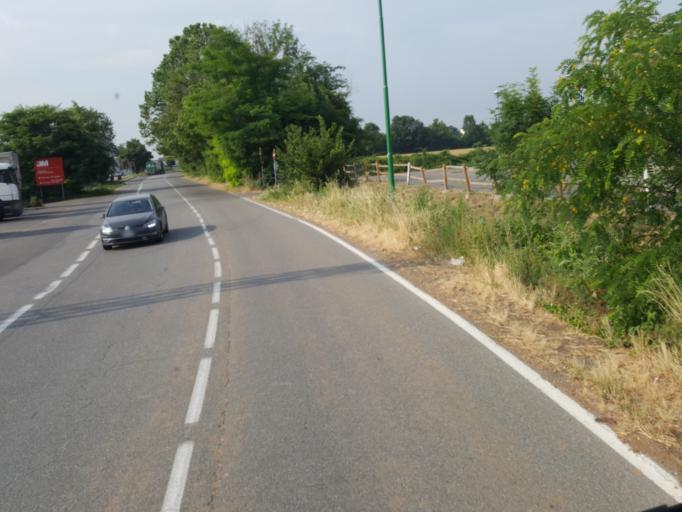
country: IT
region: Lombardy
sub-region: Provincia di Bergamo
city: Grassobbio
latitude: 45.6546
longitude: 9.7068
